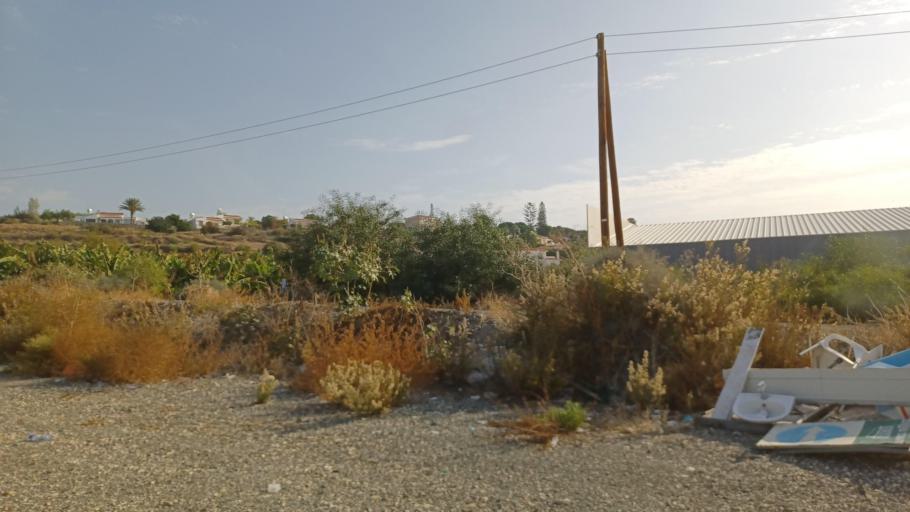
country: CY
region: Pafos
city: Pegeia
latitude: 34.8651
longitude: 32.3798
